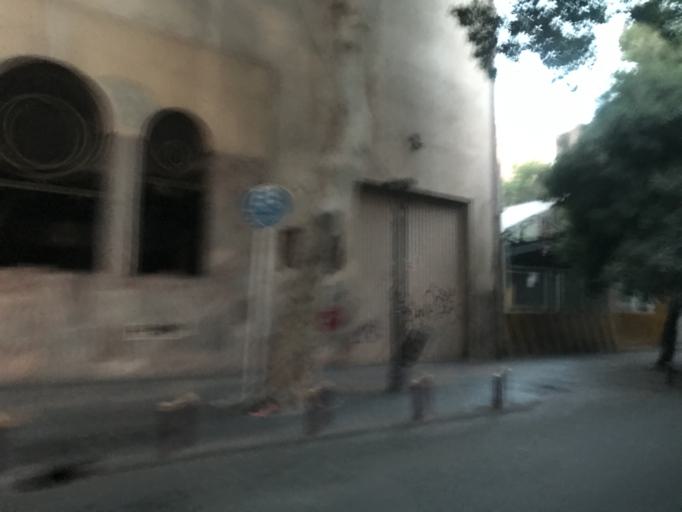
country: AR
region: Mendoza
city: Mendoza
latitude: -32.8916
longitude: -68.8383
